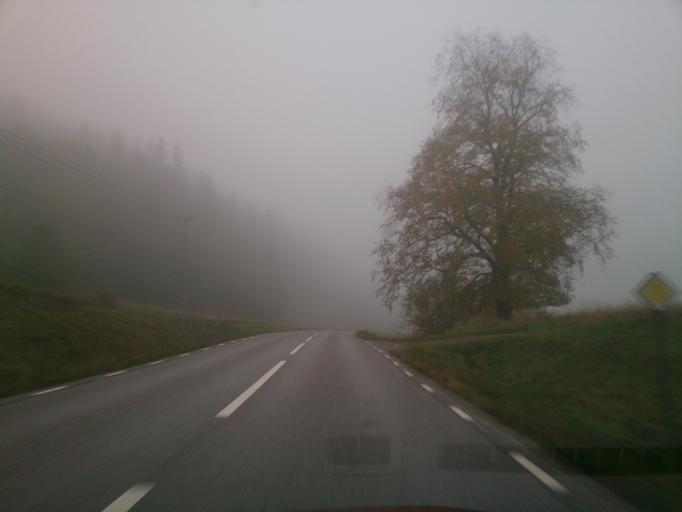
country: SE
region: OEstergoetland
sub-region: Atvidabergs Kommun
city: Atvidaberg
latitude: 58.0879
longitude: 15.8771
